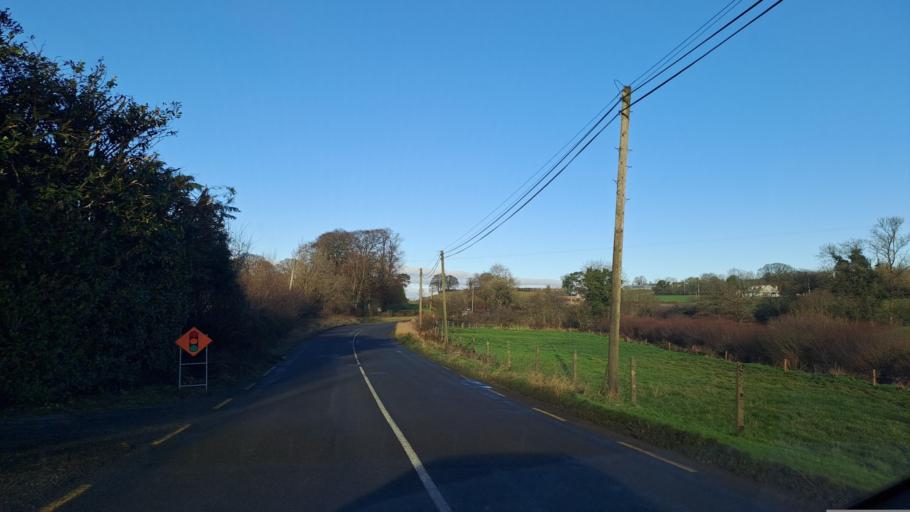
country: IE
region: Ulster
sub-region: An Cabhan
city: Bailieborough
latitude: 53.8973
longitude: -6.9674
